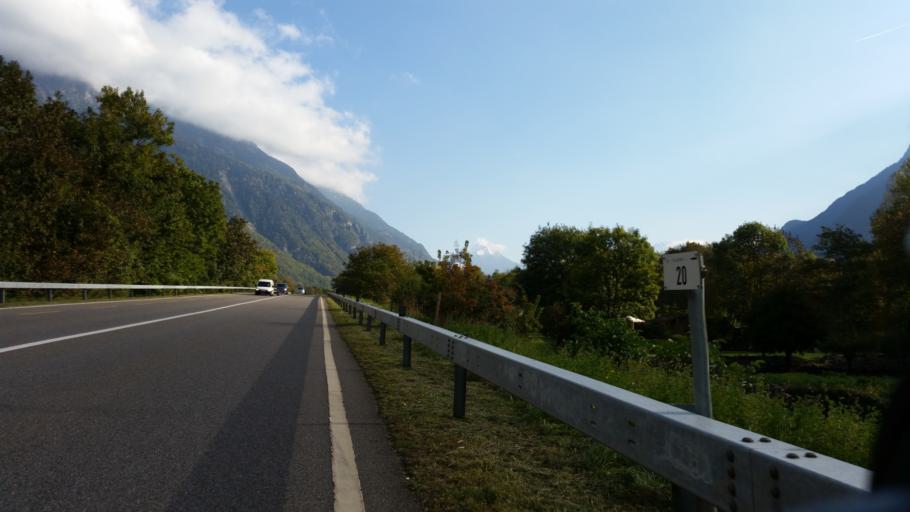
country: CH
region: Valais
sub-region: Martigny District
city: Evionnaz
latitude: 46.2009
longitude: 7.0165
